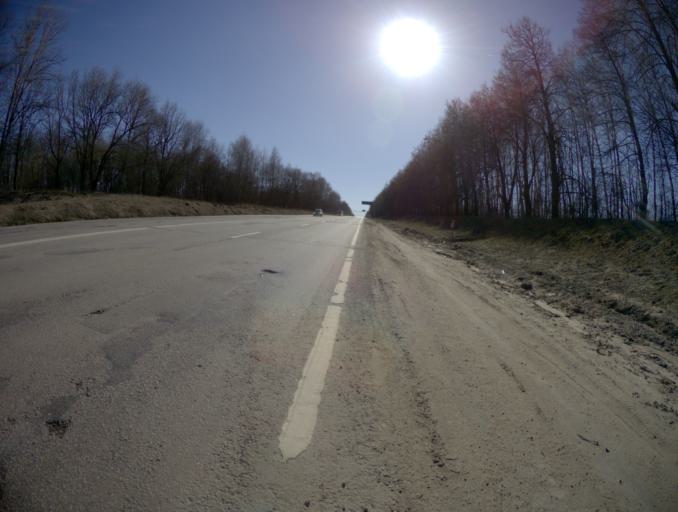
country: RU
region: Vladimir
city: Bogolyubovo
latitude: 56.1798
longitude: 40.5056
